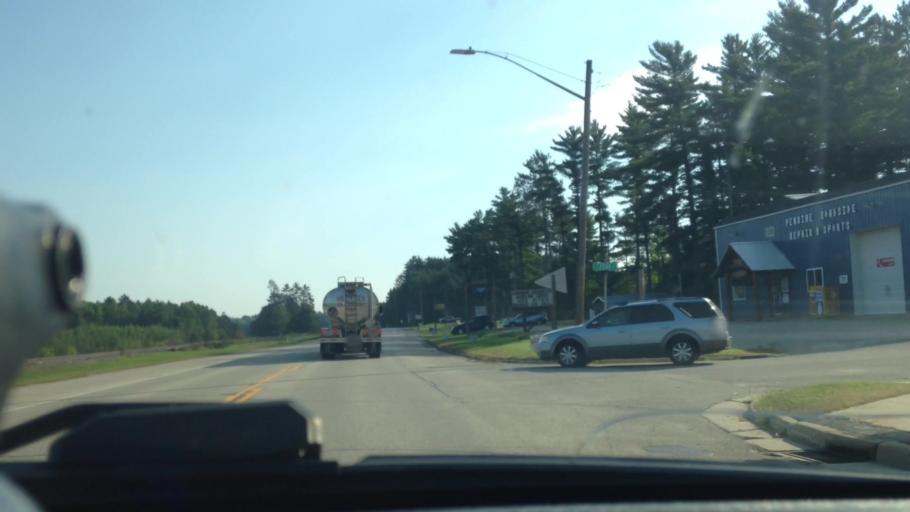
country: US
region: Wisconsin
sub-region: Marinette County
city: Niagara
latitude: 45.6362
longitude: -87.9885
